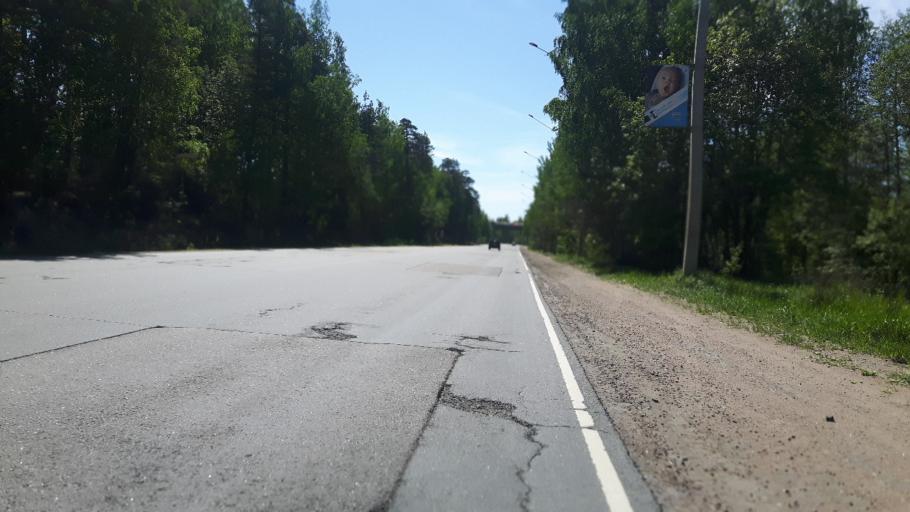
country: RU
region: Leningrad
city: Sosnovyy Bor
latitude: 59.8667
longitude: 29.0732
